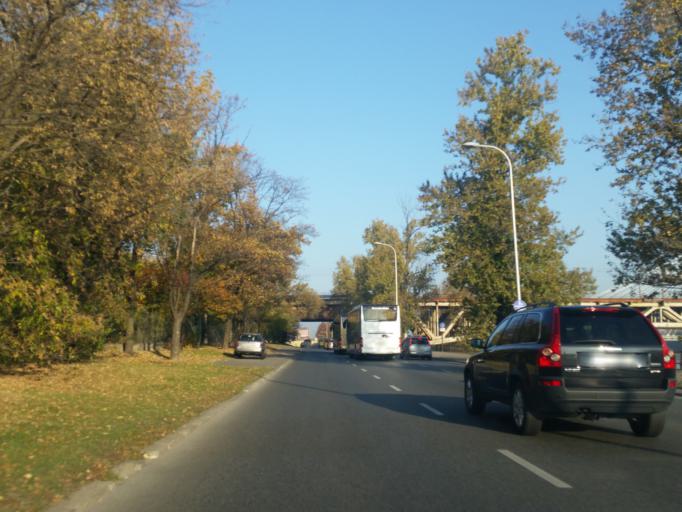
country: PL
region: Masovian Voivodeship
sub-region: Warszawa
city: Praga Polnoc
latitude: 52.2366
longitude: 21.0364
